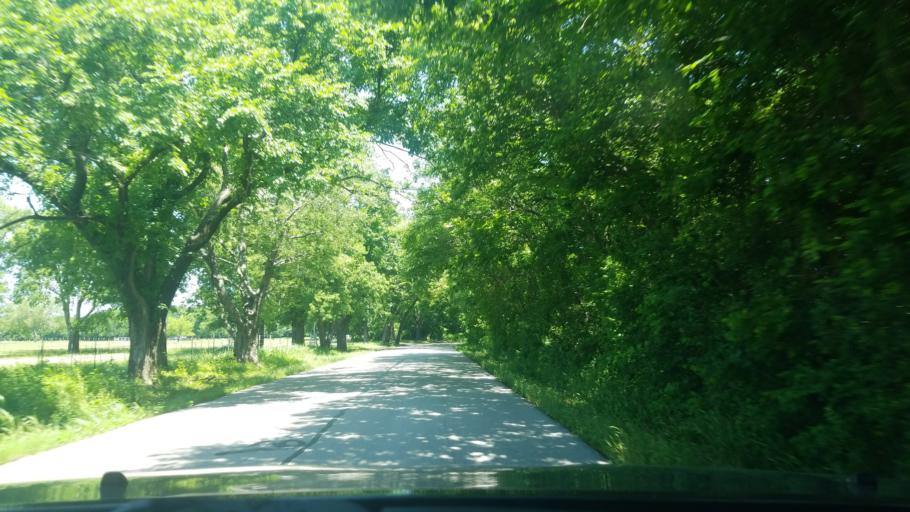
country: US
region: Texas
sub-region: Denton County
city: Sanger
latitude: 33.3451
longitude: -97.2206
